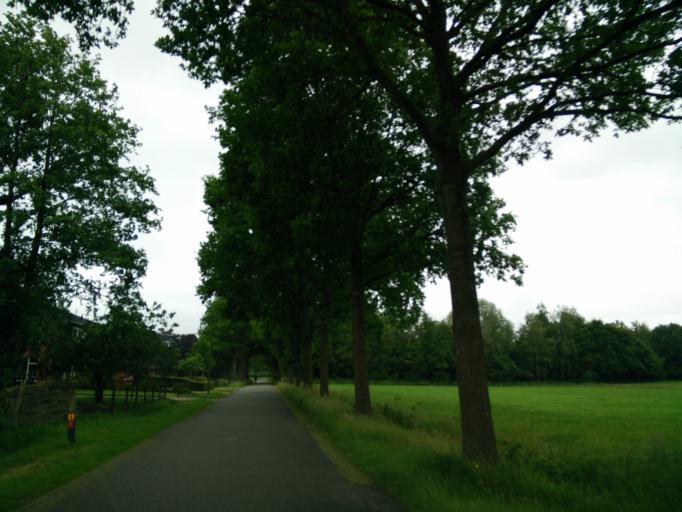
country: NL
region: Groningen
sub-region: Gemeente Leek
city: Leek
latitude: 53.1404
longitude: 6.4746
